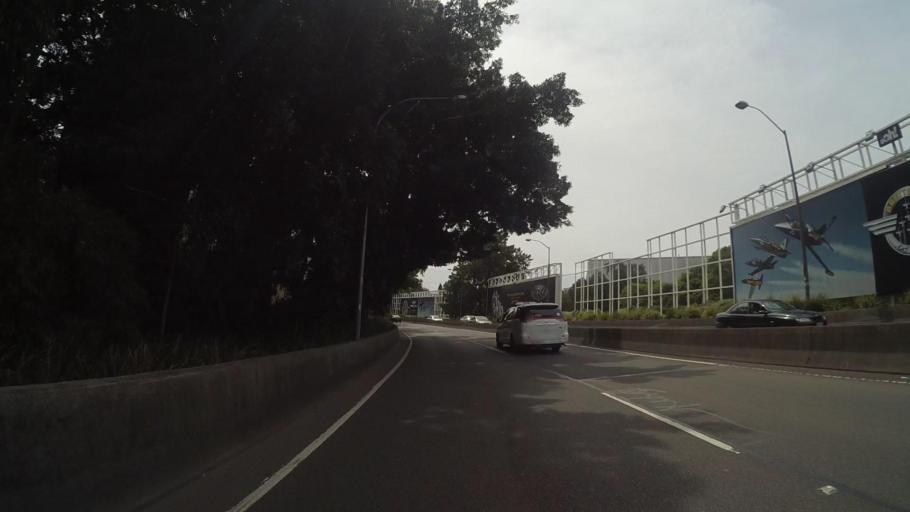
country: AU
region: New South Wales
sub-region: Botany Bay
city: Mascot
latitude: -33.9278
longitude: 151.1837
